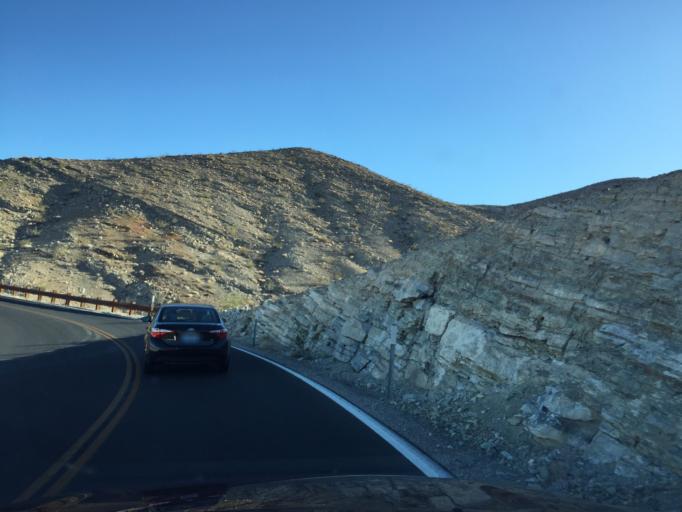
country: US
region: California
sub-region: Inyo County
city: Lone Pine
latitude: 36.3522
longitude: -117.5363
